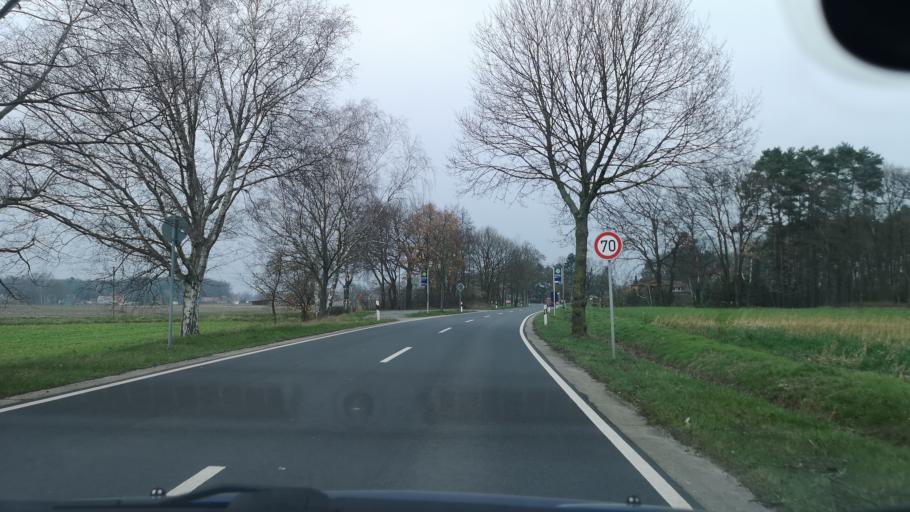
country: DE
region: Lower Saxony
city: Neustadt am Rubenberge
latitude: 52.4937
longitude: 9.5384
